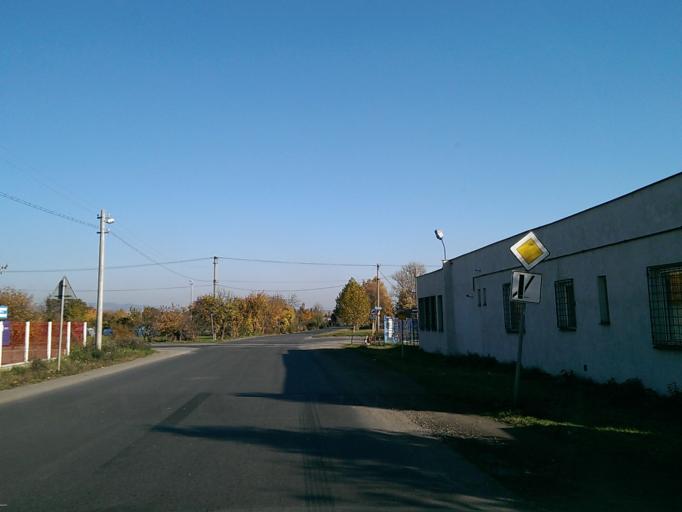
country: CZ
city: Prisovice
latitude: 50.5759
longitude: 15.0723
